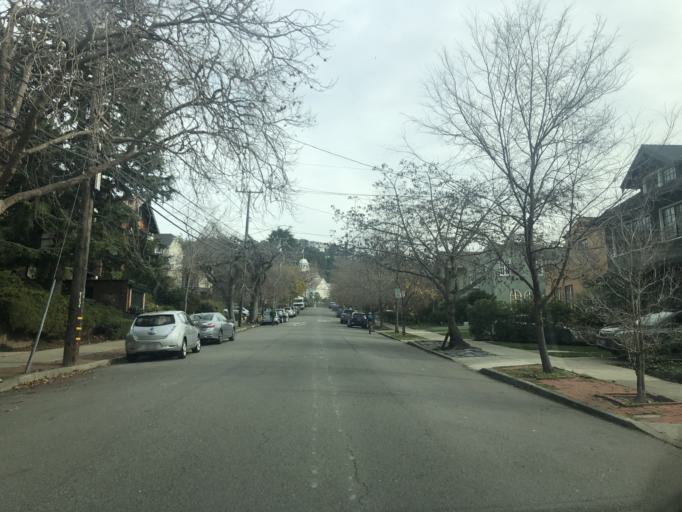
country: US
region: California
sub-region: Alameda County
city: Berkeley
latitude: 37.8588
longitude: -122.2479
